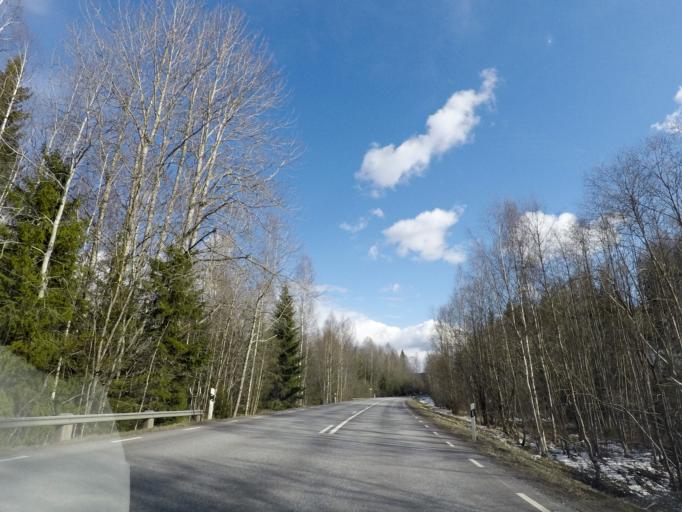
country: SE
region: Vaestmanland
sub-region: Skinnskattebergs Kommun
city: Skinnskatteberg
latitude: 59.8456
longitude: 15.6757
